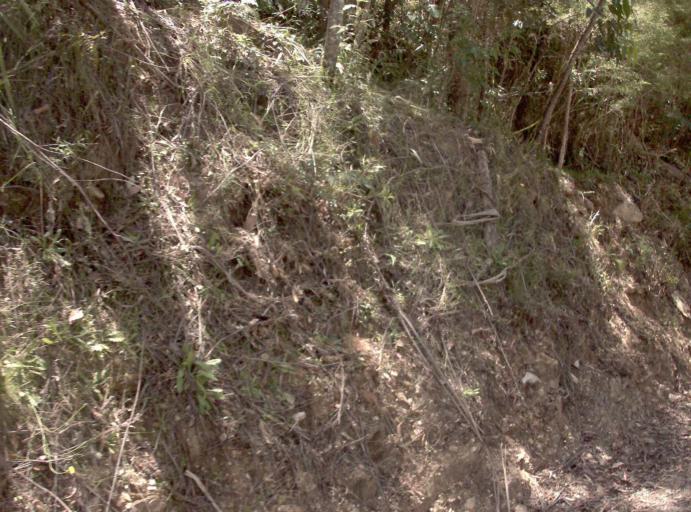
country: AU
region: New South Wales
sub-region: Bombala
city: Bombala
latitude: -37.4601
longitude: 148.9371
